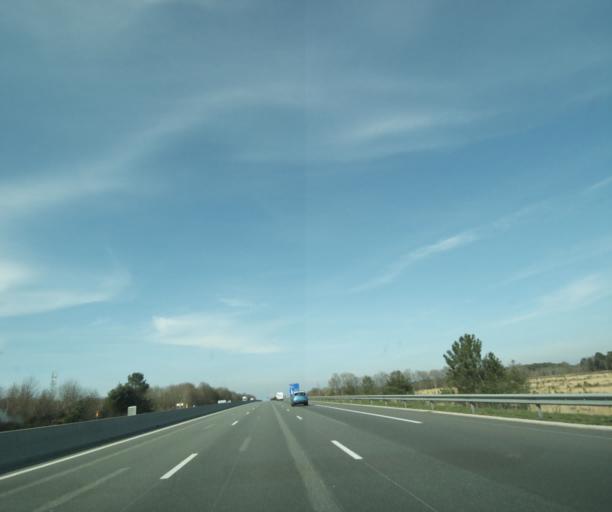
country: FR
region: Centre
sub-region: Departement du Loir-et-Cher
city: Theillay
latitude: 47.2726
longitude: 2.0426
